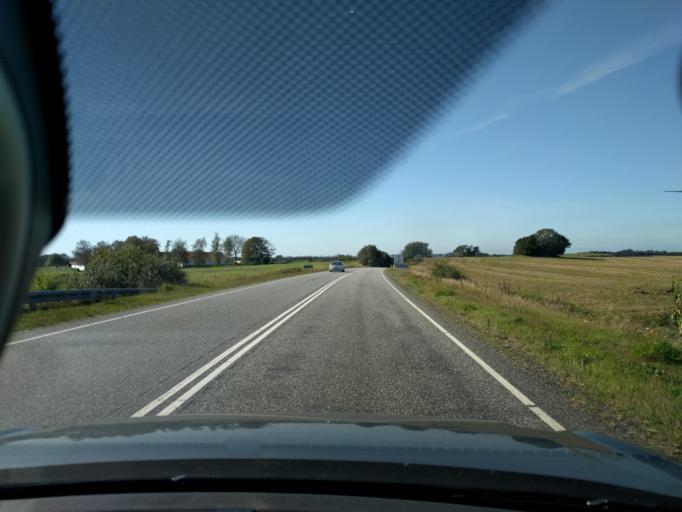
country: DK
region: North Denmark
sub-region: Mariagerfjord Kommune
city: Hobro
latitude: 56.6678
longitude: 9.7222
